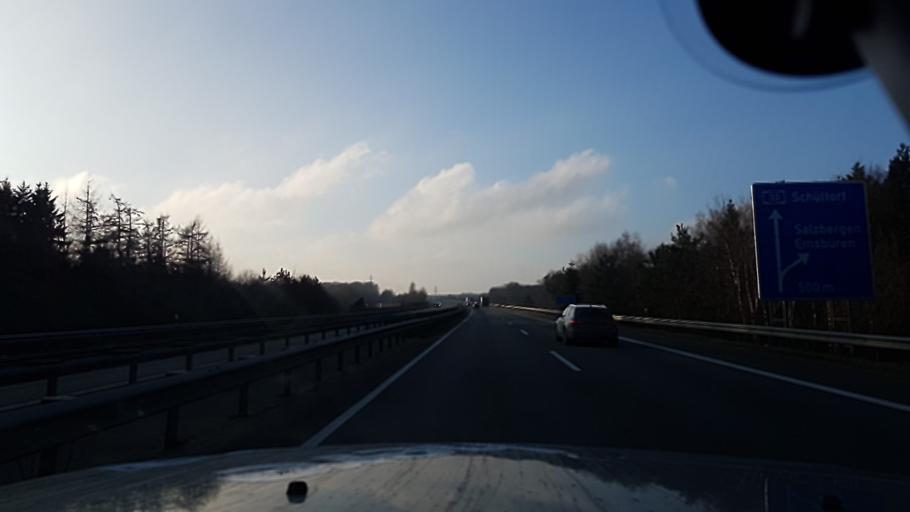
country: DE
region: Lower Saxony
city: Salzbergen
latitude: 52.3450
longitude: 7.3531
